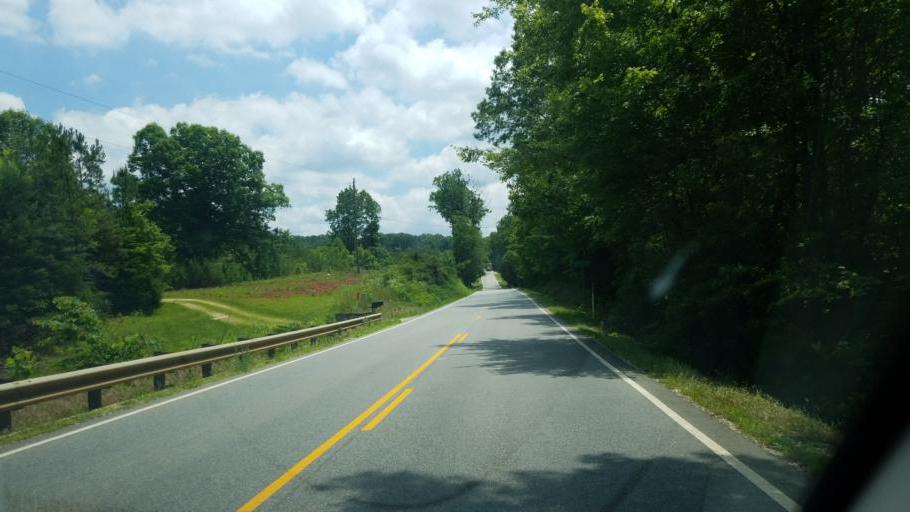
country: US
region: Virginia
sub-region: Nelson County
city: Lovingston
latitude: 37.5694
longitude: -78.8531
